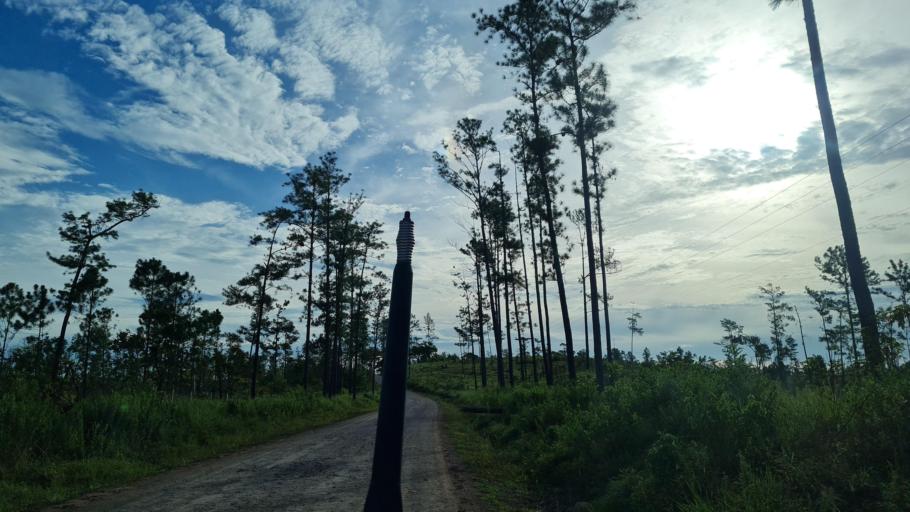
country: NI
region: Atlantico Sur
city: La Cruz de Rio Grande
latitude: 13.5563
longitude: -84.2971
